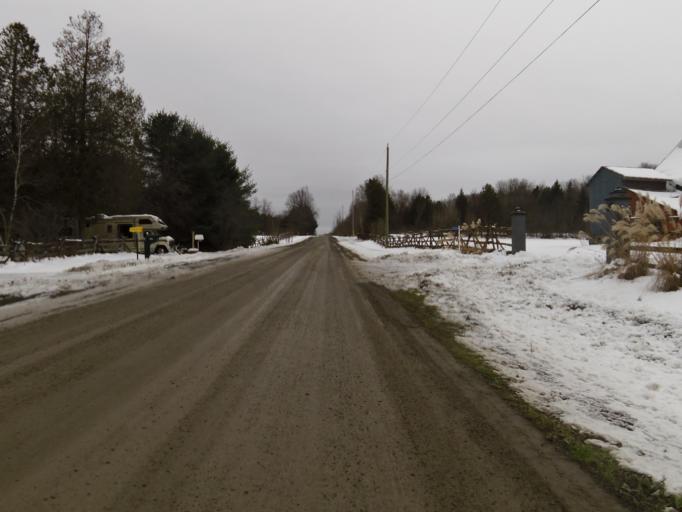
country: CA
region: Ontario
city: Carleton Place
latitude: 45.1408
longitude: -76.2517
